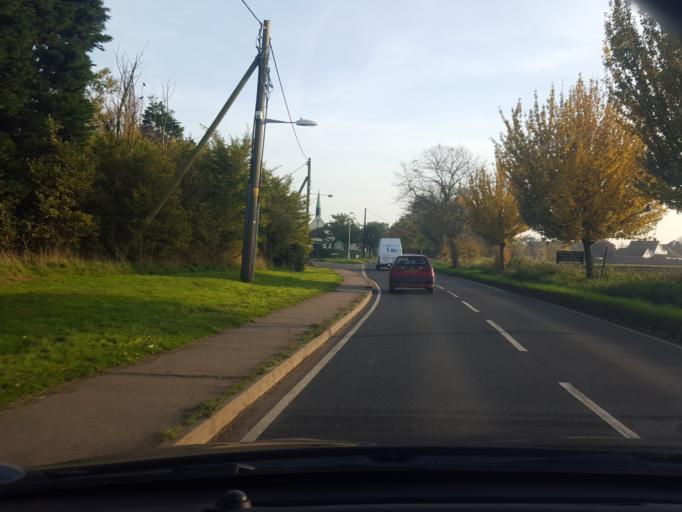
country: GB
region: England
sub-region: Essex
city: Frinton-on-Sea
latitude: 51.8313
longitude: 1.2097
